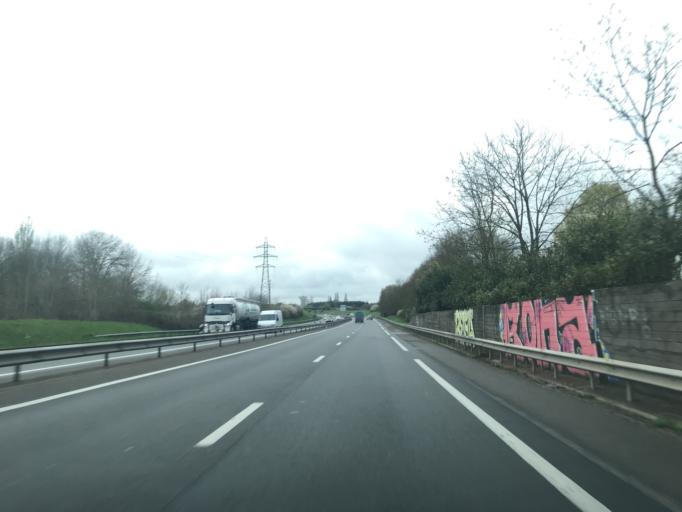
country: FR
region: Centre
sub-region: Departement du Loiret
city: Boigny-sur-Bionne
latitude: 47.9174
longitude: 2.0076
